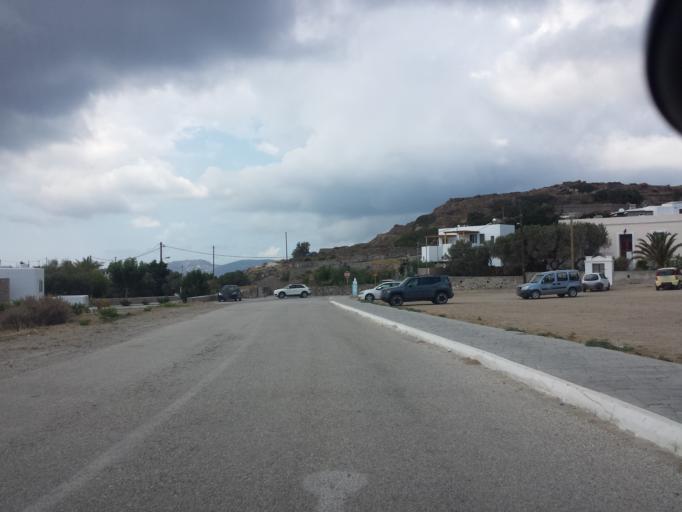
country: GR
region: South Aegean
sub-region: Nomos Kykladon
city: Milos
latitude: 36.7430
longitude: 24.4246
